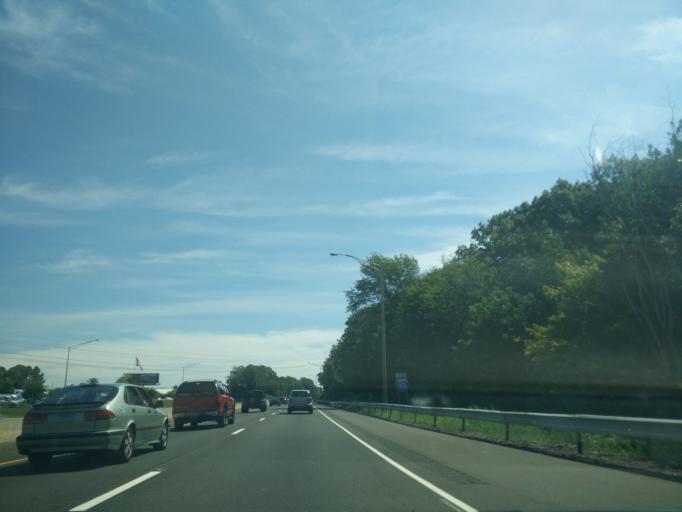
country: US
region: Connecticut
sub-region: New Haven County
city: North Branford
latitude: 41.2961
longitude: -72.7581
